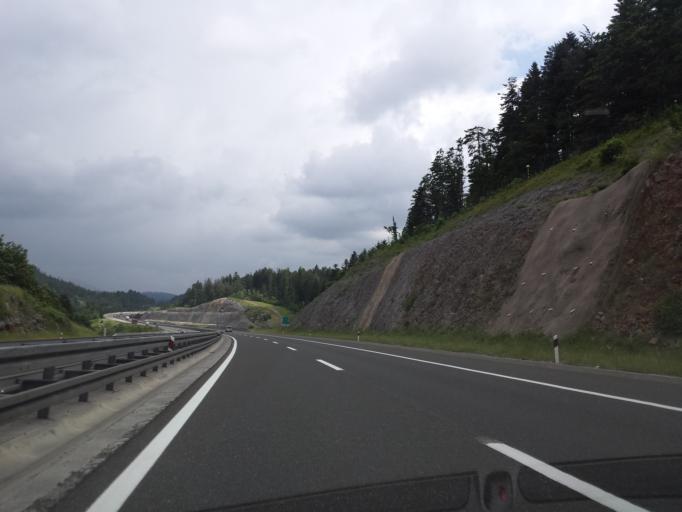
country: HR
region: Primorsko-Goranska
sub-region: Grad Delnice
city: Delnice
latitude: 45.3489
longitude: 14.7574
